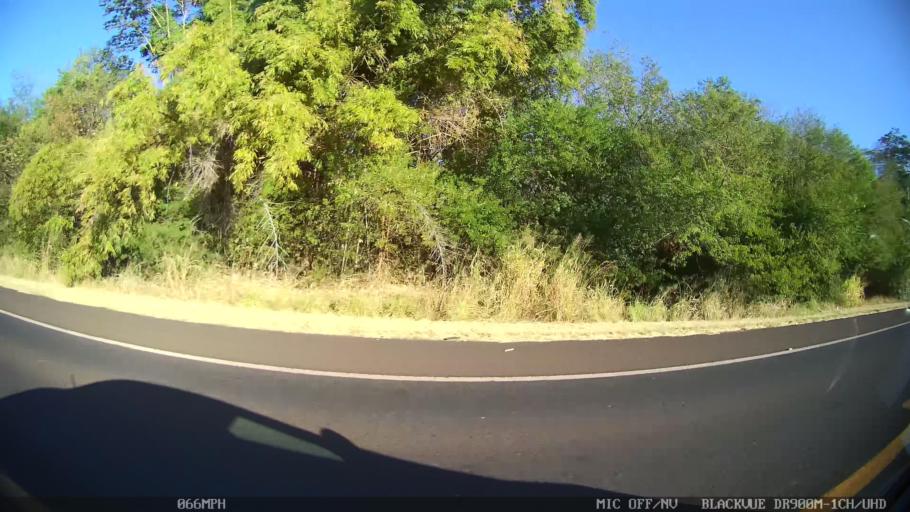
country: BR
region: Sao Paulo
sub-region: Olimpia
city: Olimpia
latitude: -20.7126
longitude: -48.9832
